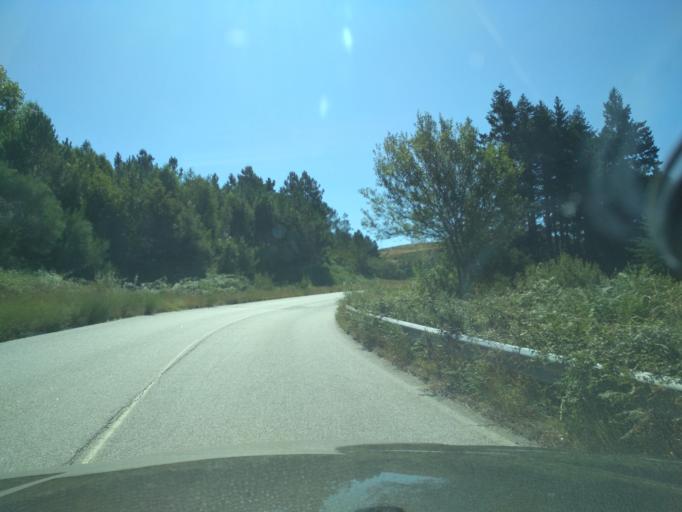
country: PT
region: Vila Real
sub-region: Ribeira de Pena
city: Ribeira de Pena
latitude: 41.5023
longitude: -7.7754
